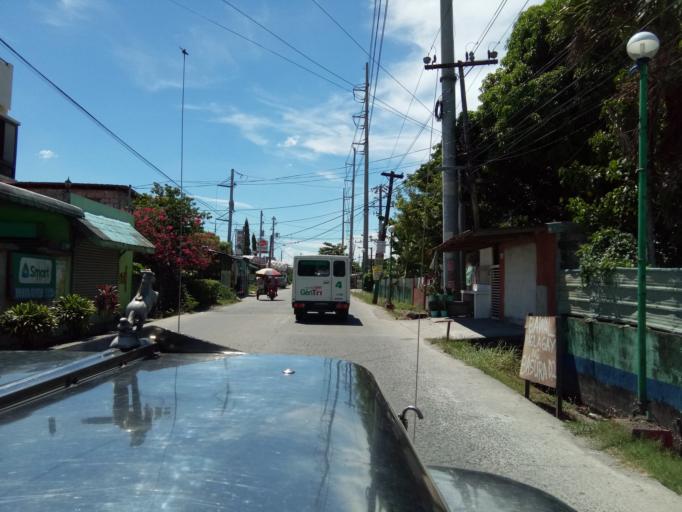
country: PH
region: Calabarzon
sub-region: Province of Cavite
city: General Trias
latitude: 14.3668
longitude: 120.8926
